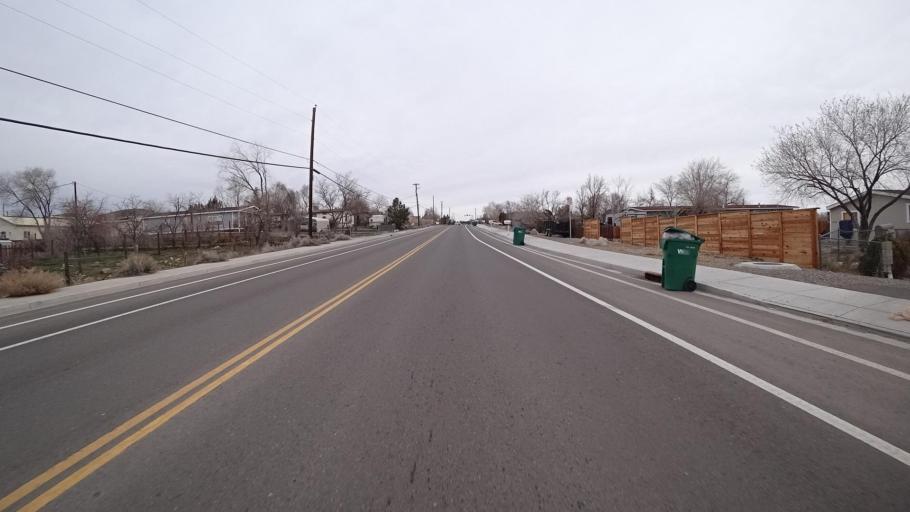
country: US
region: Nevada
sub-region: Washoe County
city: Sun Valley
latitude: 39.6021
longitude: -119.7807
